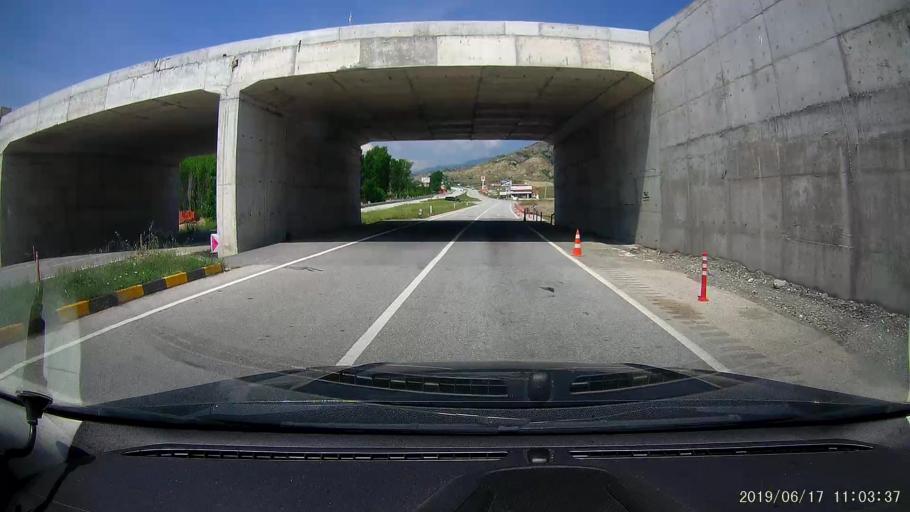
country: TR
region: Kastamonu
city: Tosya
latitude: 41.0185
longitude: 34.1125
